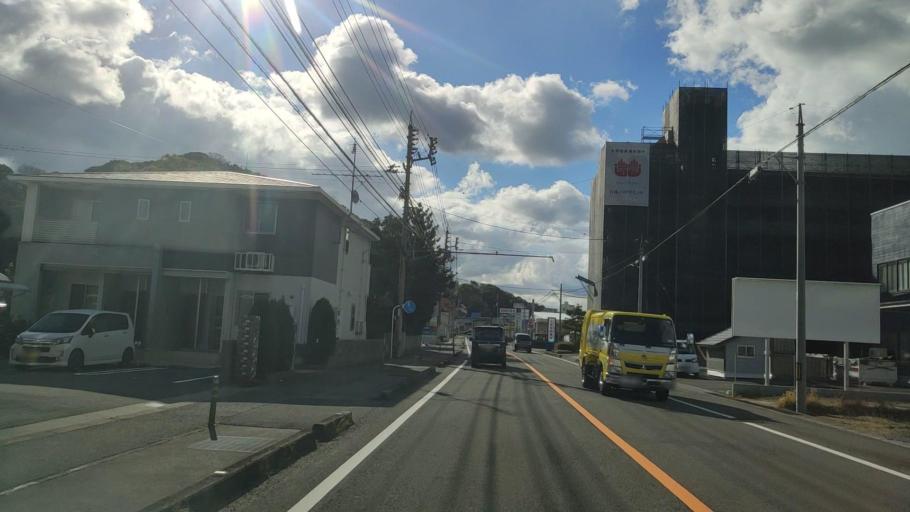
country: JP
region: Ehime
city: Masaki-cho
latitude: 33.8346
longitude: 132.7092
